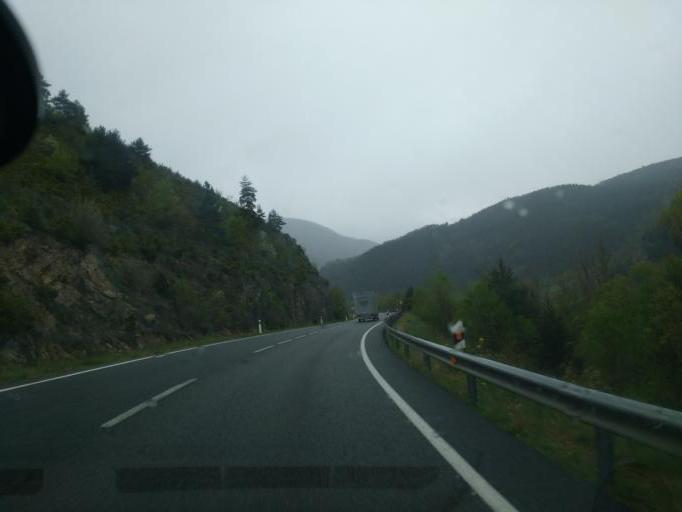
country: ES
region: Catalonia
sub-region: Provincia de Lleida
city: Lles de Cerdanya
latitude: 42.3637
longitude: 1.6816
